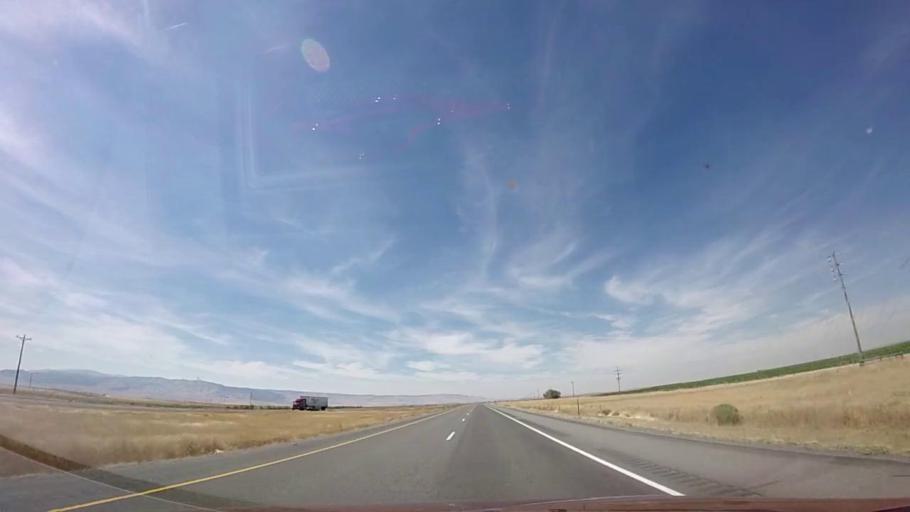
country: US
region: Idaho
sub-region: Minidoka County
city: Rupert
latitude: 42.3416
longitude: -113.2323
